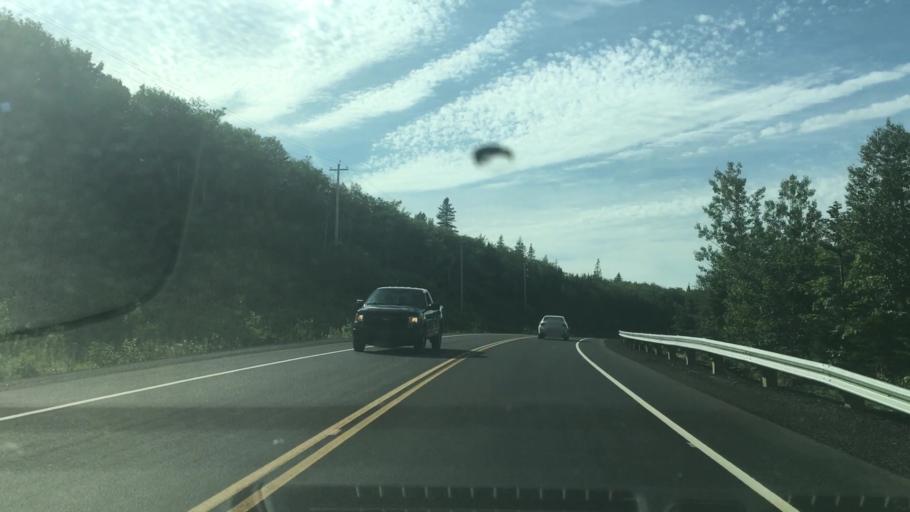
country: CA
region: Nova Scotia
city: Sydney Mines
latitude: 46.8371
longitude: -60.3825
